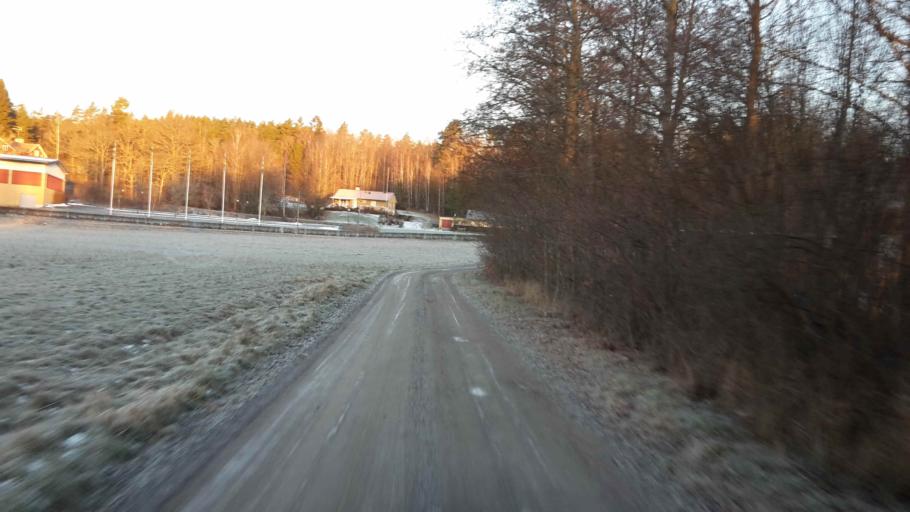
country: SE
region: OEstergoetland
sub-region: Soderkopings Kommun
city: Soederkoeping
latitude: 58.2797
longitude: 16.2168
